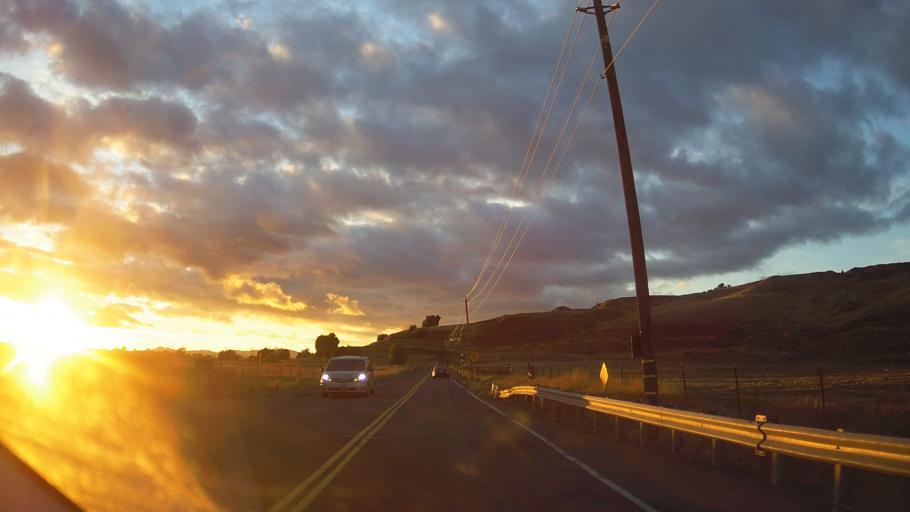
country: US
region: California
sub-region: Solano County
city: Fairfield
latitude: 38.2872
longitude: -121.9907
